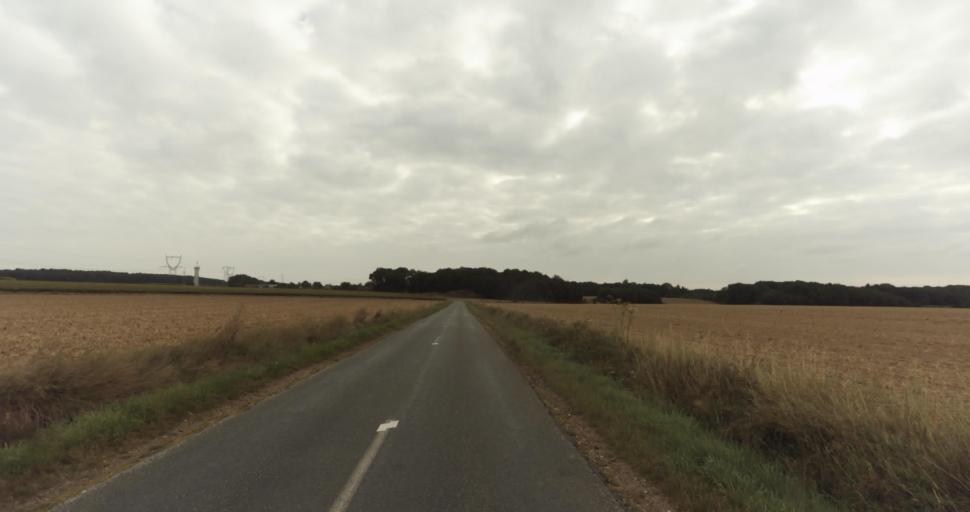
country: FR
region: Haute-Normandie
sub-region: Departement de l'Eure
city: Marcilly-sur-Eure
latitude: 48.8598
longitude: 1.3318
